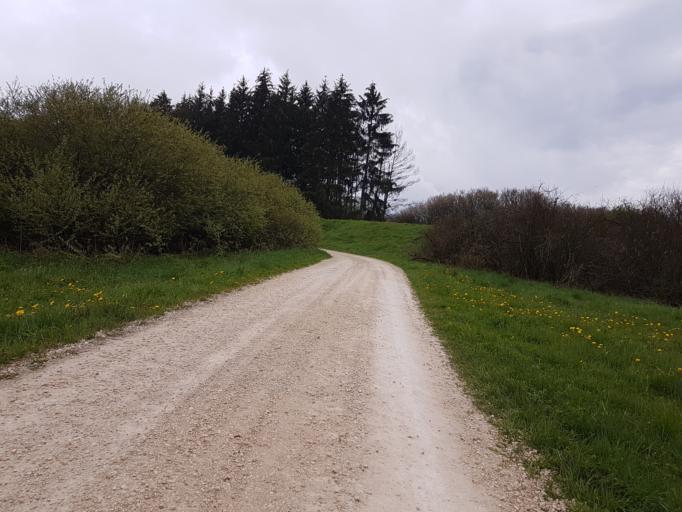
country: DE
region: Baden-Wuerttemberg
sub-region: Freiburg Region
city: Blumberg
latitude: 47.8440
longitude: 8.5725
